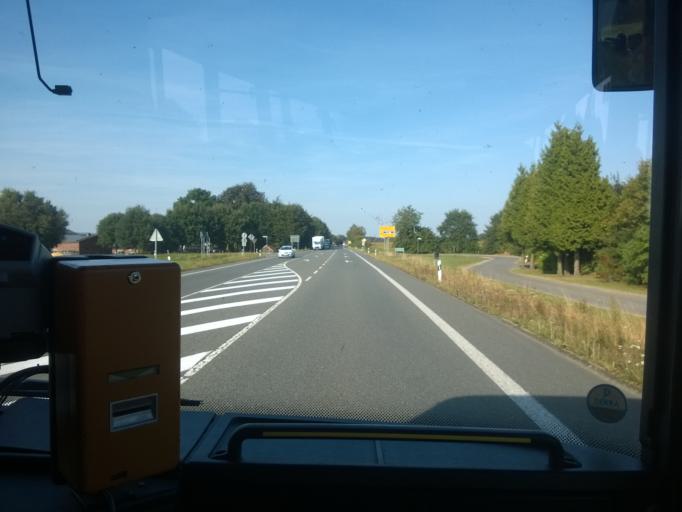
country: DE
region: North Rhine-Westphalia
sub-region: Regierungsbezirk Munster
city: Sudlohn
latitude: 51.9317
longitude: 6.8542
